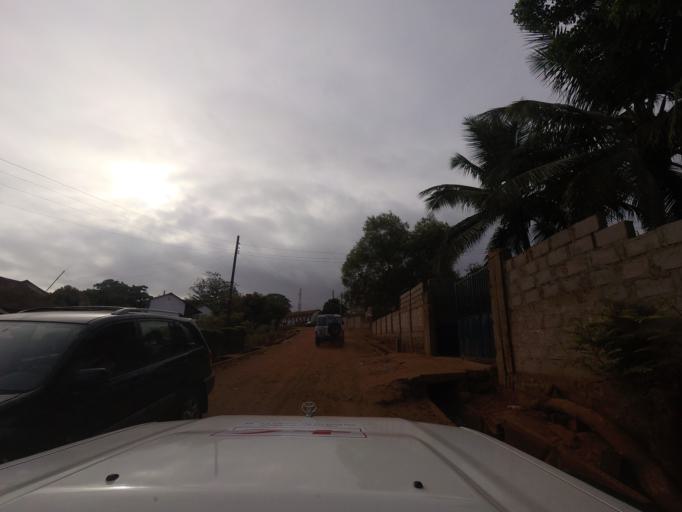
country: SL
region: Western Area
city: Freetown
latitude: 8.4896
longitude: -13.2690
